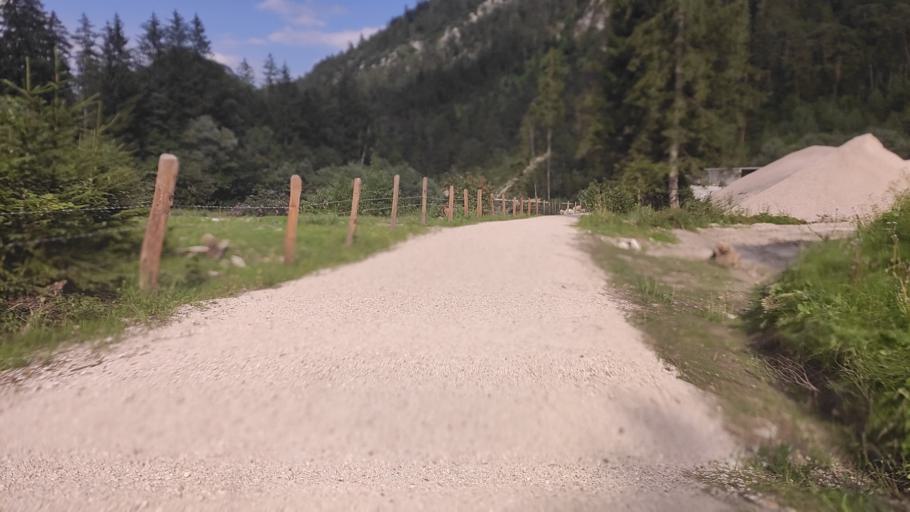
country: DE
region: Bavaria
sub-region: Upper Bavaria
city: Schneizlreuth
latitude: 47.6656
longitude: 12.7698
